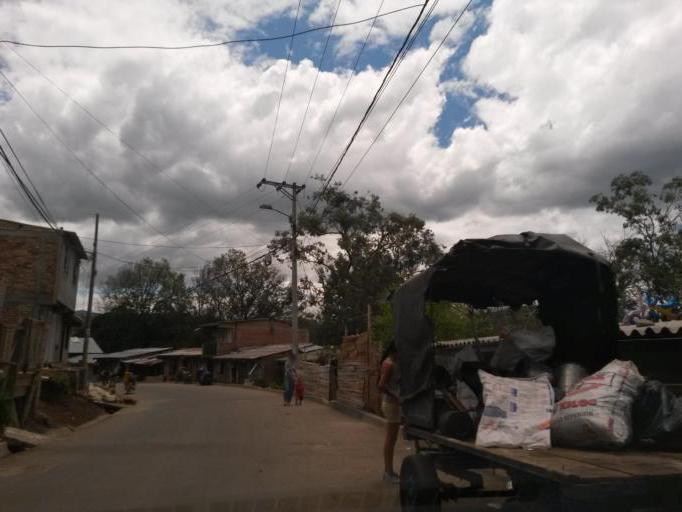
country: CO
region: Cauca
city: Popayan
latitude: 2.4775
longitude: -76.5663
